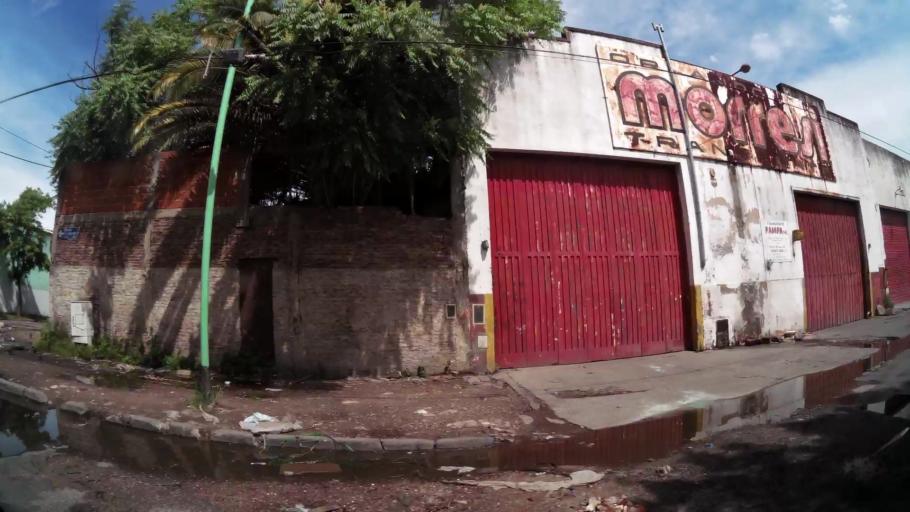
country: AR
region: Buenos Aires F.D.
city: Villa Lugano
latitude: -34.6645
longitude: -58.4338
